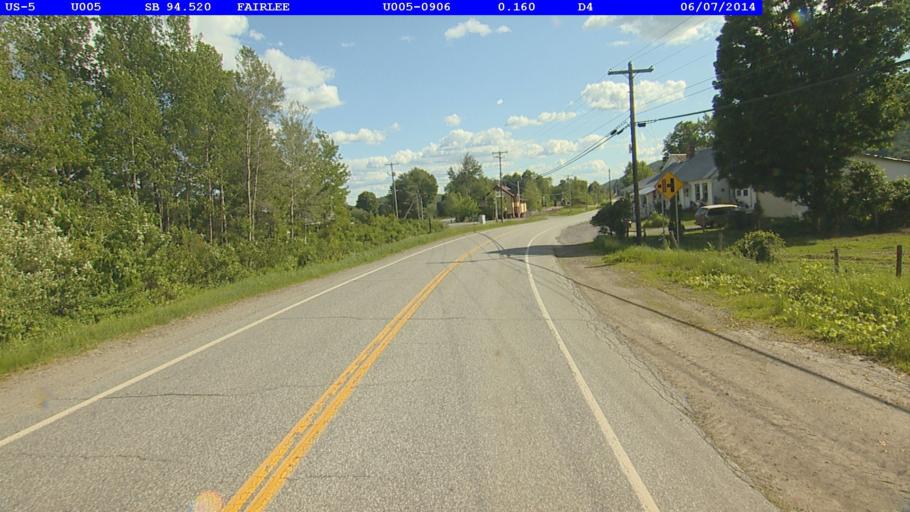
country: US
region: New Hampshire
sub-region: Grafton County
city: Orford
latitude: 43.8763
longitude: -72.1763
